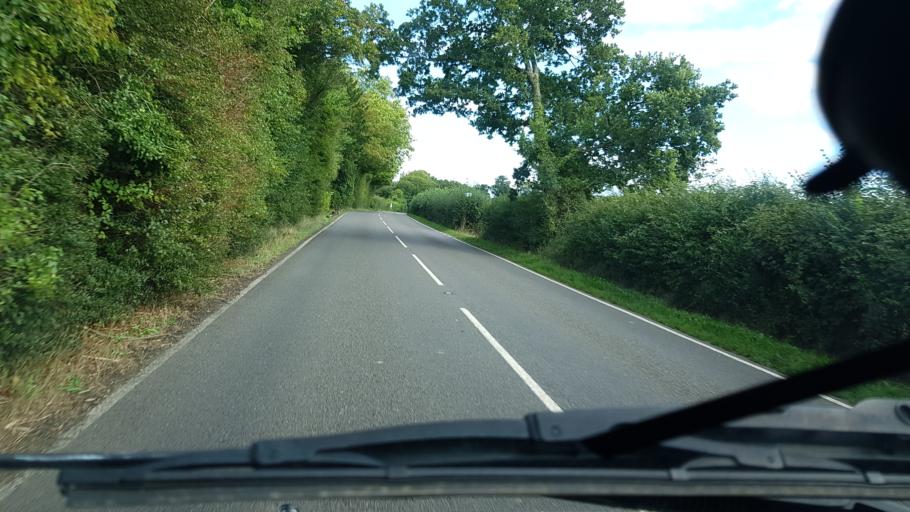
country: GB
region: England
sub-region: Surrey
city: Ockley
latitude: 51.0947
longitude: -0.3837
